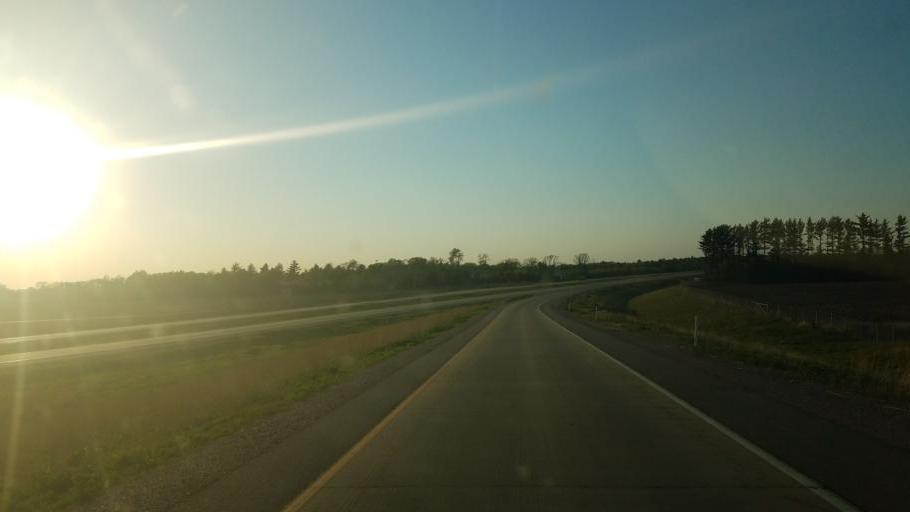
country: US
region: Wisconsin
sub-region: Sauk County
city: West Baraboo
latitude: 43.5161
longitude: -89.7838
